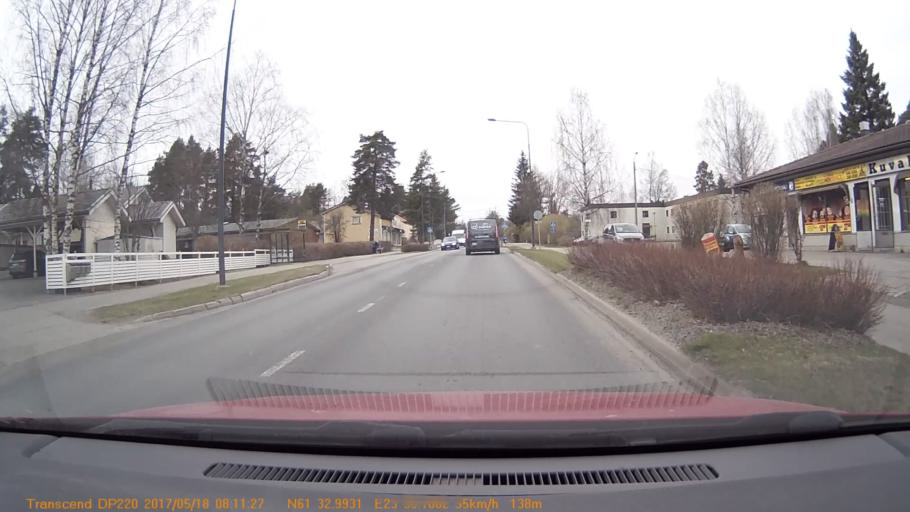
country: FI
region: Pirkanmaa
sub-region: Tampere
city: Yloejaervi
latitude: 61.5499
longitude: 23.5854
